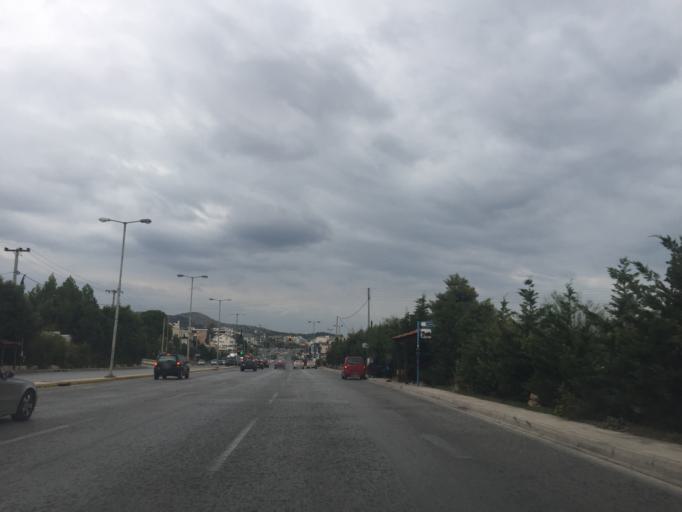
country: GR
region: Attica
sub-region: Nomarchia Anatolikis Attikis
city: Voula
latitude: 37.8462
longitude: 23.7697
